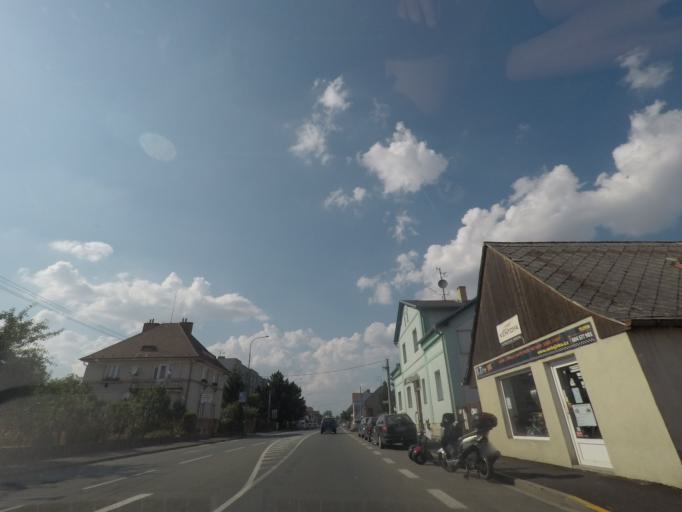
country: CZ
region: Kralovehradecky
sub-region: Okres Nachod
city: Jaromer
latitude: 50.3493
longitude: 15.9112
